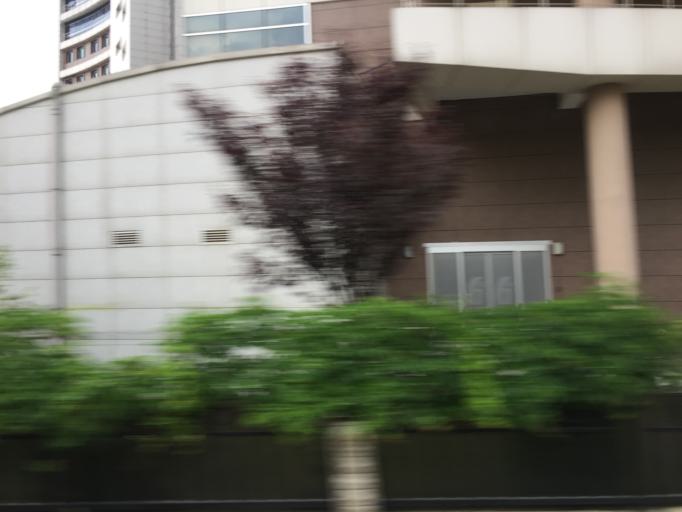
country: TR
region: Gaziantep
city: Gaziantep
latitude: 37.0679
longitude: 37.3737
